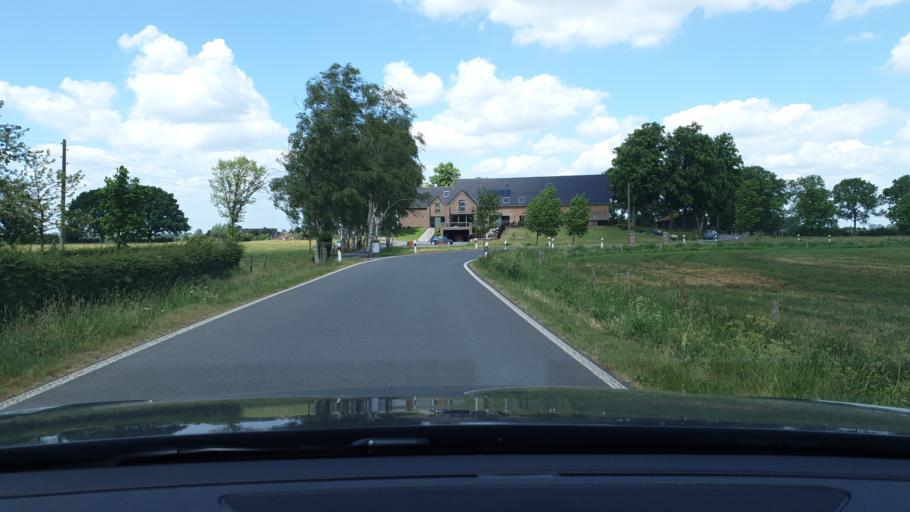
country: DE
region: North Rhine-Westphalia
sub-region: Regierungsbezirk Dusseldorf
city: Kranenburg
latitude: 51.8164
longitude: 6.0448
